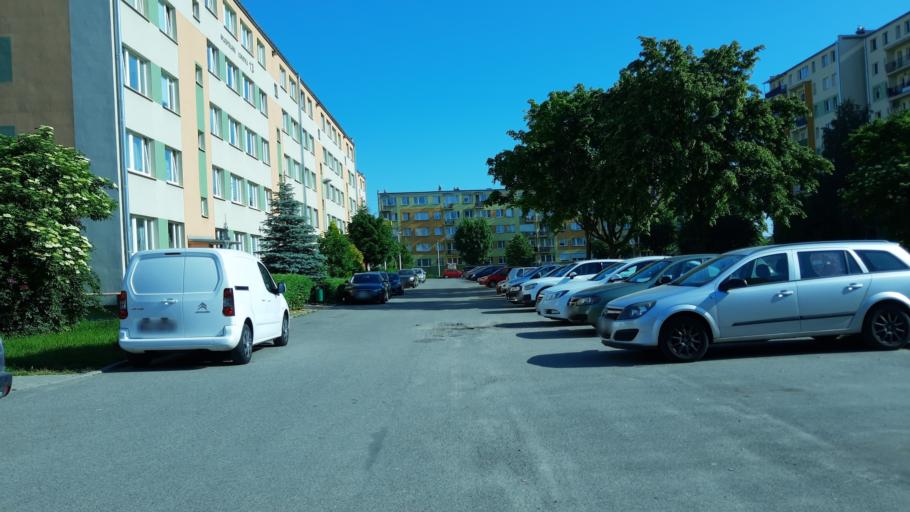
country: PL
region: Lodz Voivodeship
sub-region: Powiat sieradzki
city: Sieradz
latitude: 51.5923
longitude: 18.7225
